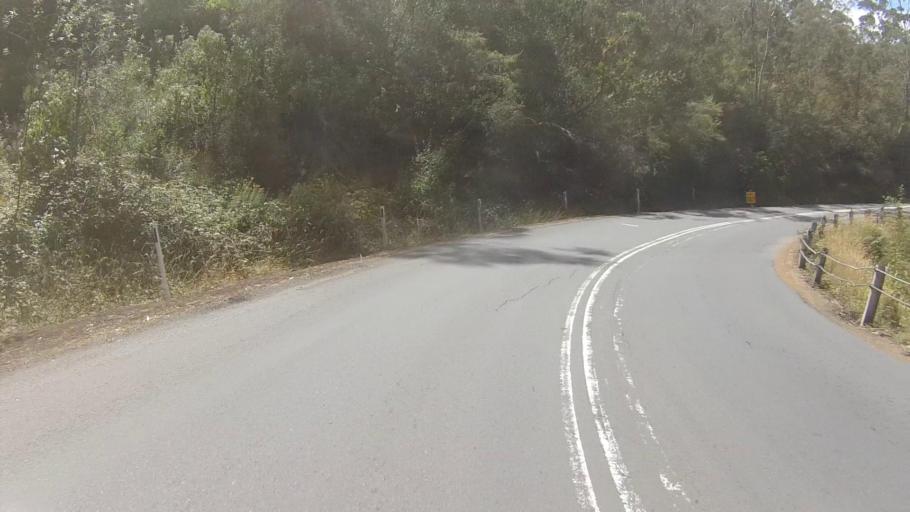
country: AU
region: Tasmania
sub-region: Kingborough
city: Taroona
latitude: -42.9596
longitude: 147.3315
